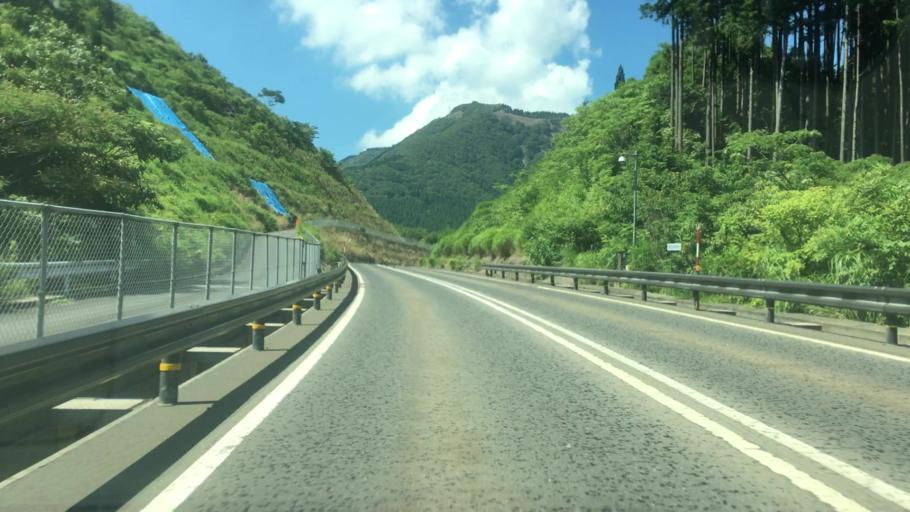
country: JP
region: Tottori
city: Tottori
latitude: 35.2827
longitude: 134.2266
